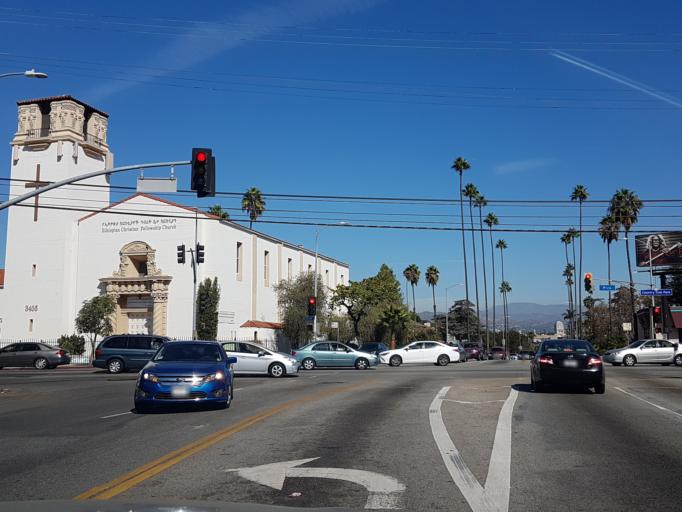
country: US
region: California
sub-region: Los Angeles County
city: Hollywood
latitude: 34.0468
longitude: -118.3177
